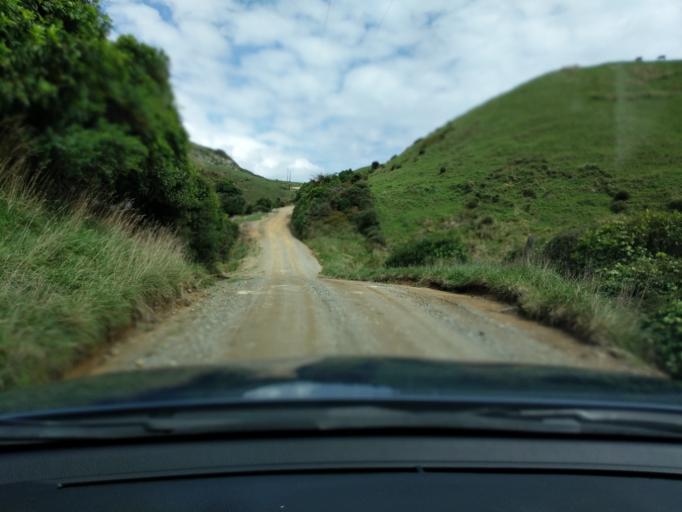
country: NZ
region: Tasman
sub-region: Tasman District
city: Takaka
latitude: -40.6569
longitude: 172.4172
